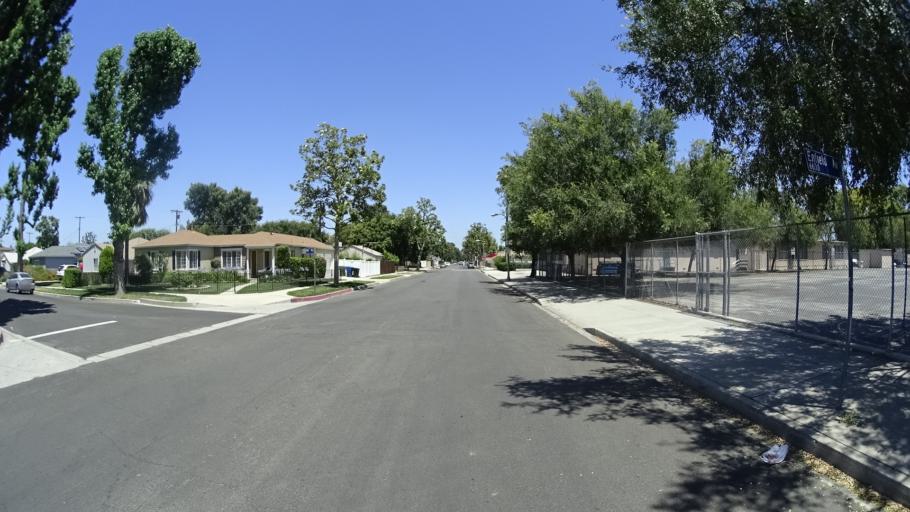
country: US
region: California
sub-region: Los Angeles County
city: Northridge
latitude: 34.1902
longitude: -118.5236
